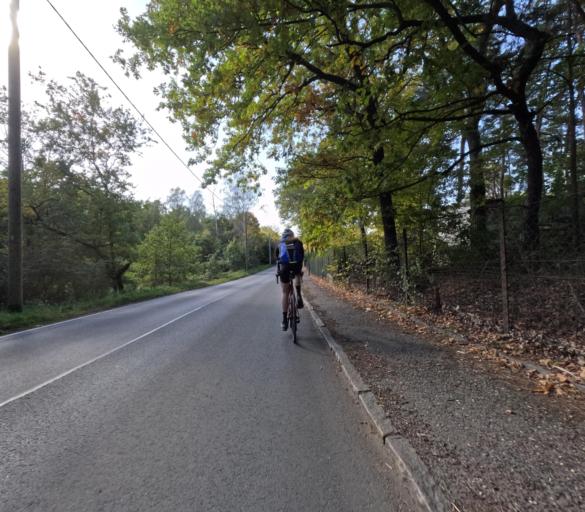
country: DE
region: Saxony
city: Radebeul
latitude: 51.1303
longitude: 13.6397
